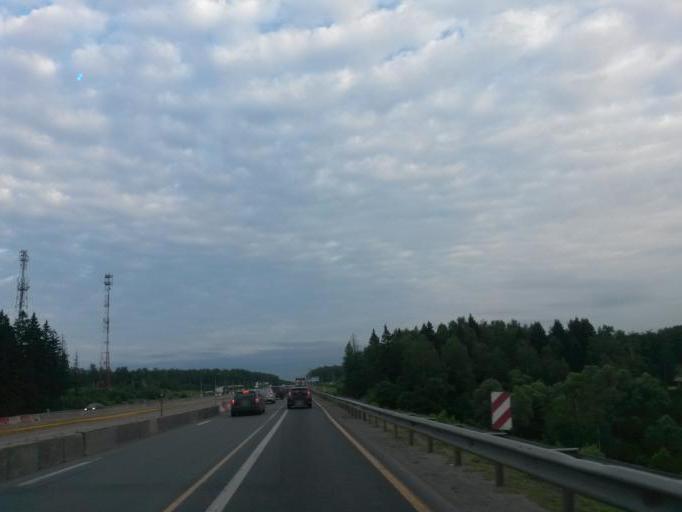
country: RU
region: Moskovskaya
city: Lyubuchany
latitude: 55.2337
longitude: 37.5280
